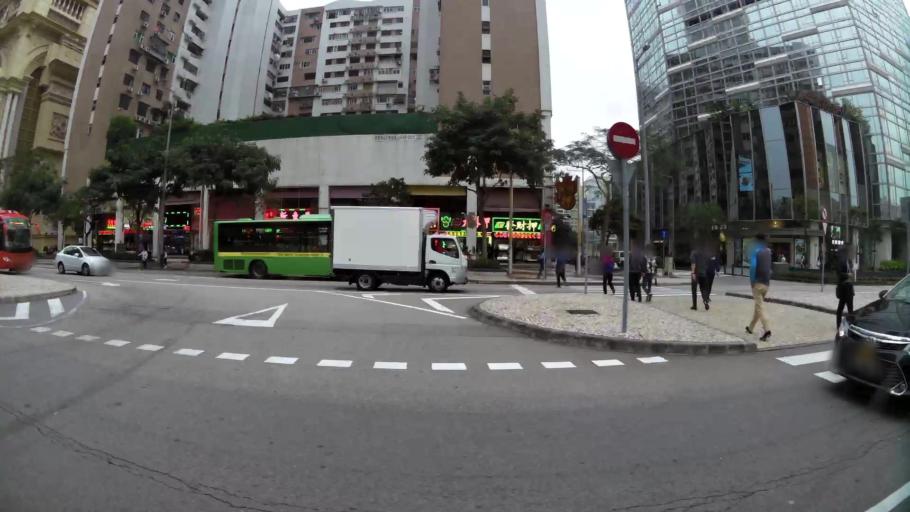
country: MO
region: Macau
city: Macau
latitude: 22.1872
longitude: 113.5484
